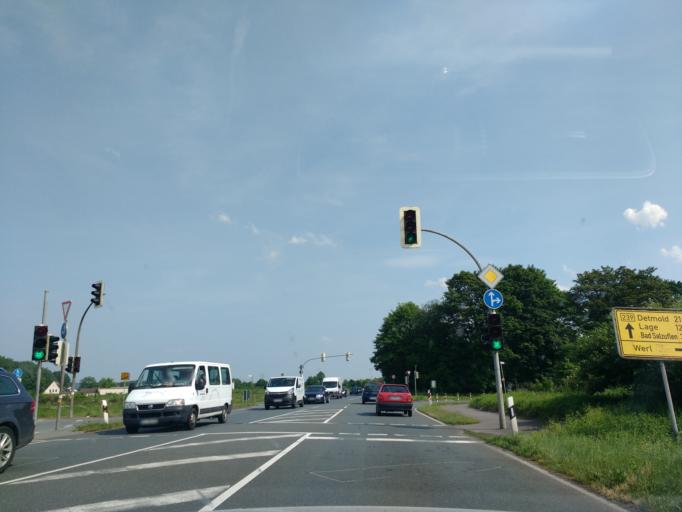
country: DE
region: North Rhine-Westphalia
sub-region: Regierungsbezirk Detmold
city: Bad Salzuflen
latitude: 52.0783
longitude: 8.7252
